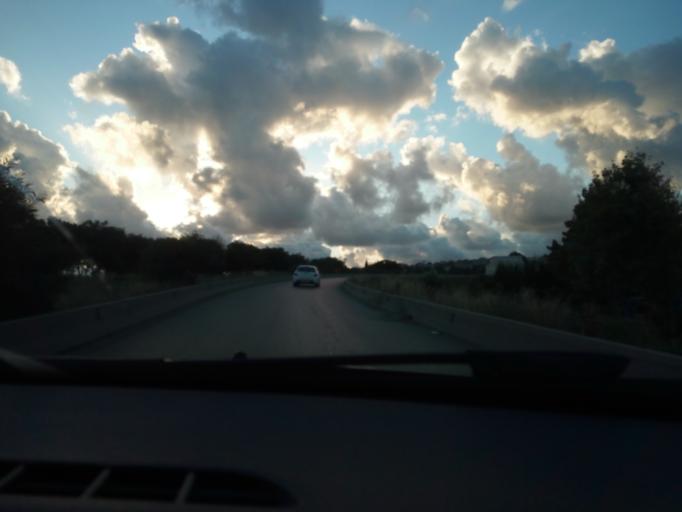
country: DZ
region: Tipaza
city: Saoula
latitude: 36.6526
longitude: 3.0129
